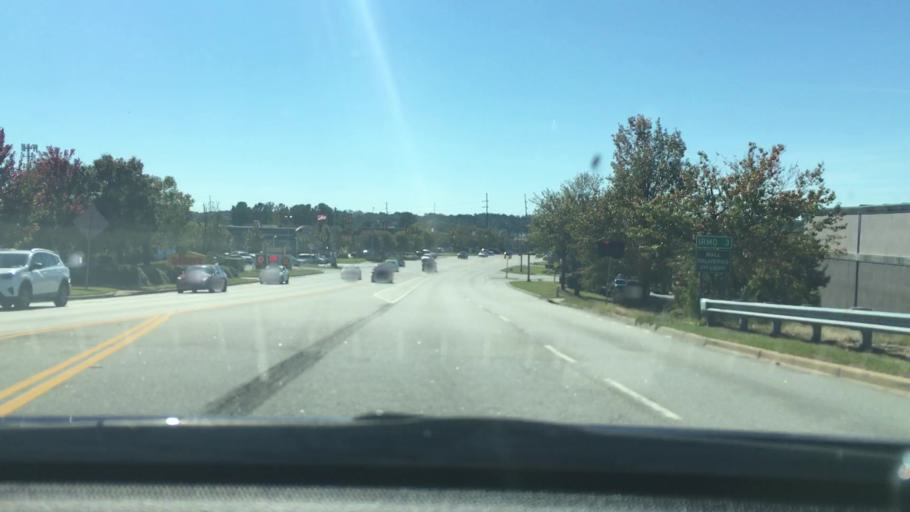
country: US
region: South Carolina
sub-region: Lexington County
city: Seven Oaks
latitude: 34.0757
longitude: -81.1545
